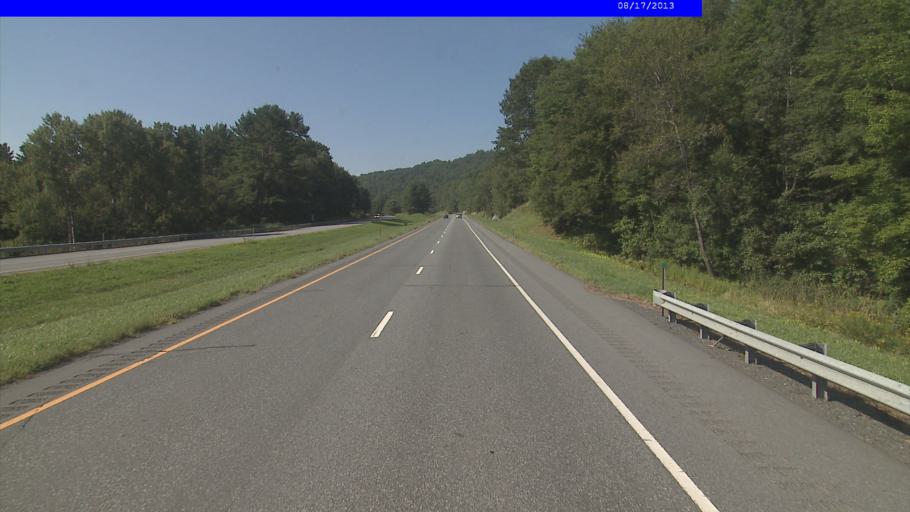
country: US
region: Vermont
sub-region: Windsor County
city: White River Junction
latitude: 43.5813
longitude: -72.3808
